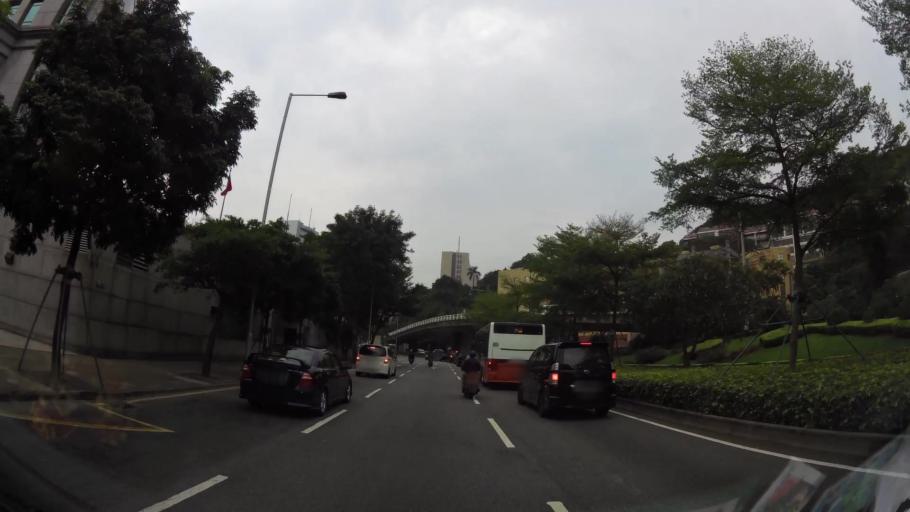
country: MO
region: Macau
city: Macau
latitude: 22.1962
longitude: 113.5528
